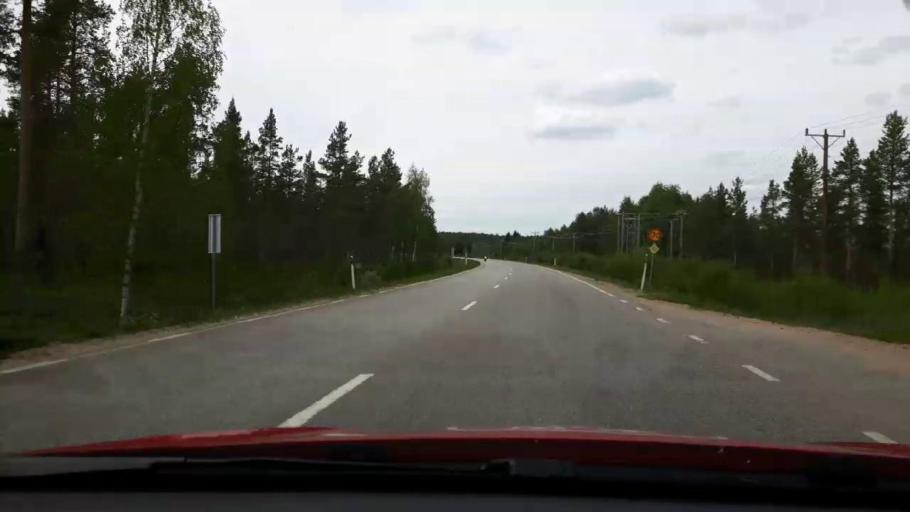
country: SE
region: Jaemtland
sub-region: Harjedalens Kommun
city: Sveg
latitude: 62.0441
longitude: 14.3535
